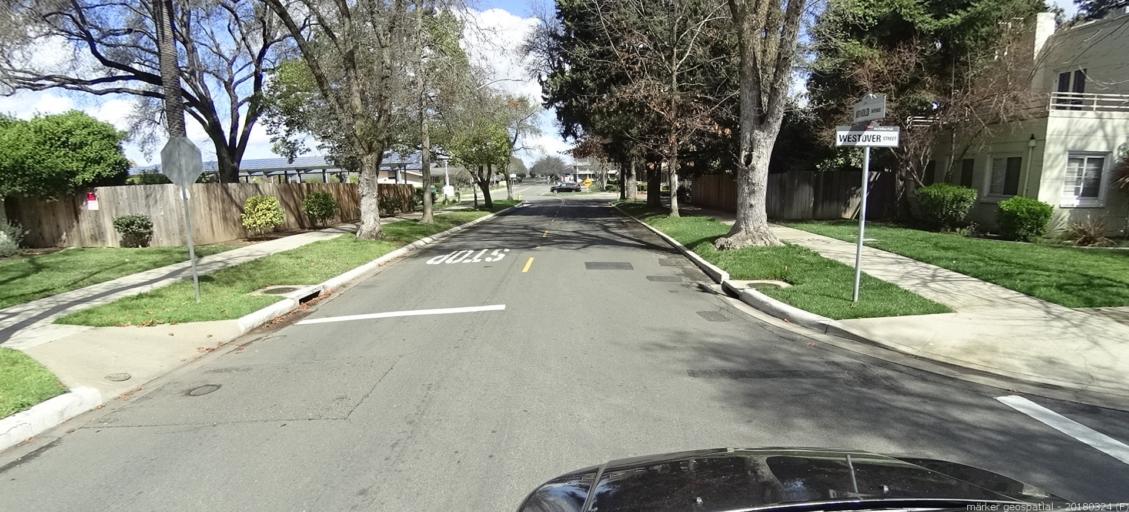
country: US
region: California
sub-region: Sacramento County
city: North Highlands
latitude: 38.6639
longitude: -121.3852
